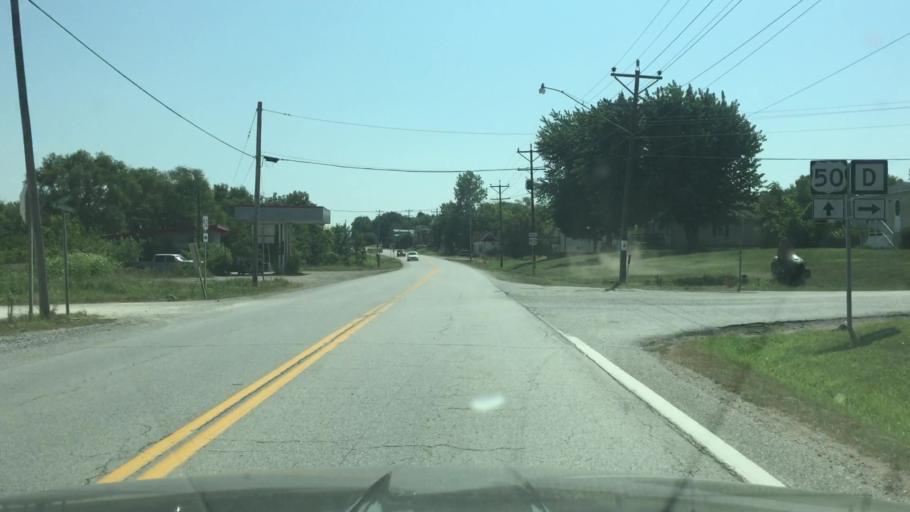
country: US
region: Missouri
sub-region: Moniteau County
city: Tipton
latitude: 38.6694
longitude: -92.8774
